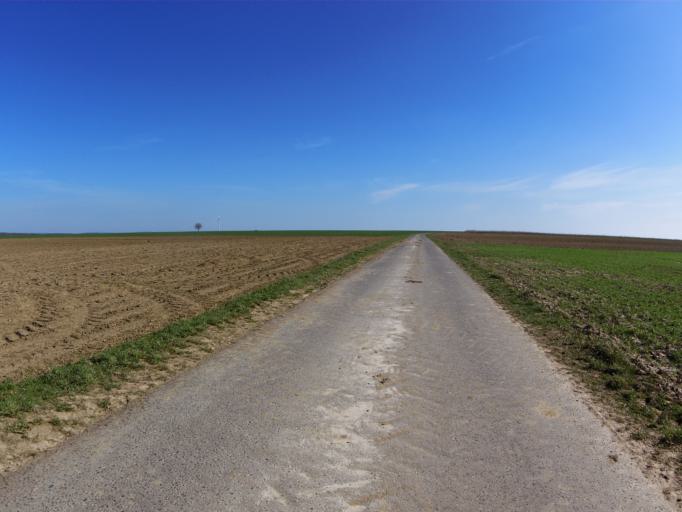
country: DE
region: Bavaria
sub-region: Regierungsbezirk Unterfranken
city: Prosselsheim
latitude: 49.8535
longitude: 10.1150
